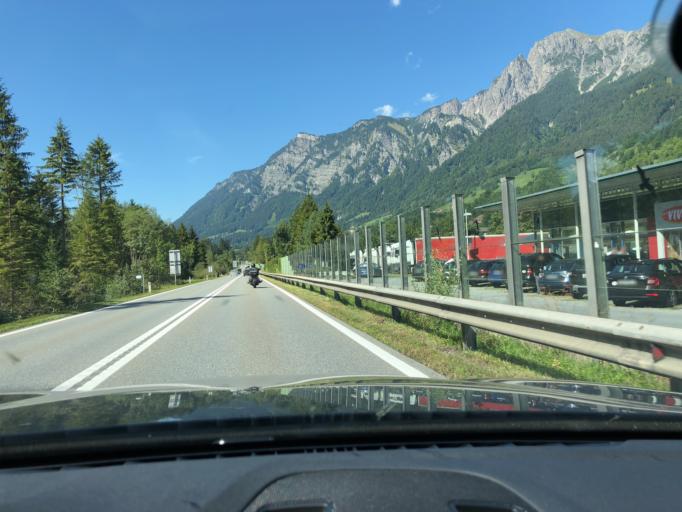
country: AT
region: Vorarlberg
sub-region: Politischer Bezirk Bludenz
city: Innerbraz
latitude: 47.1405
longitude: 9.9254
